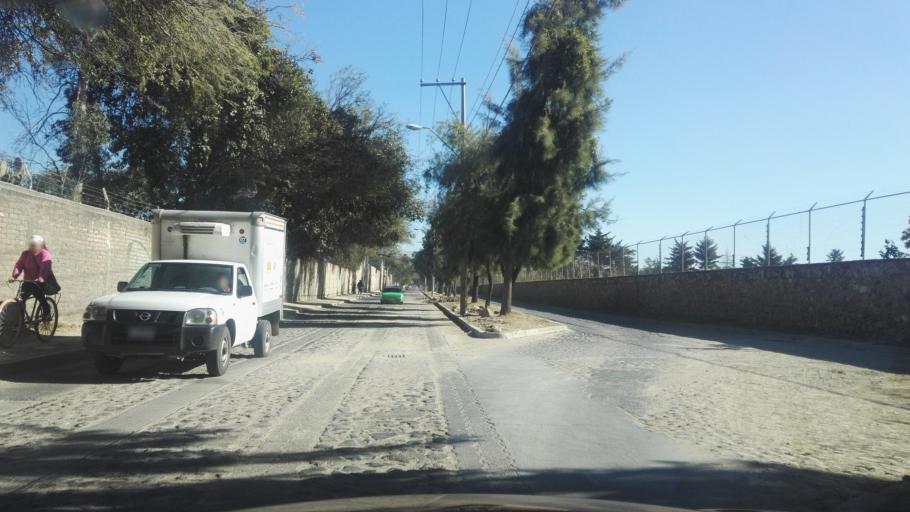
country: MX
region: Guanajuato
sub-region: Leon
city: Fraccionamiento Paraiso Real
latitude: 21.0897
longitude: -101.6098
